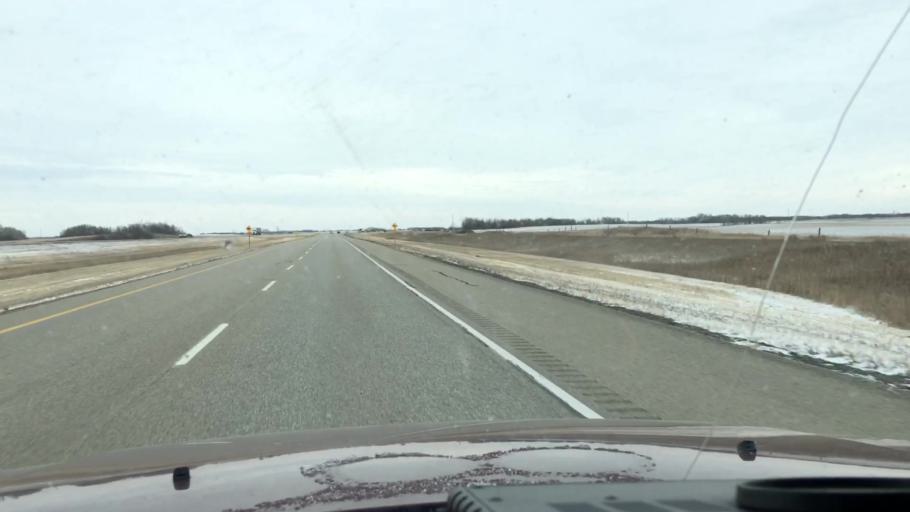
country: CA
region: Saskatchewan
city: Watrous
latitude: 51.3378
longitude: -106.0922
